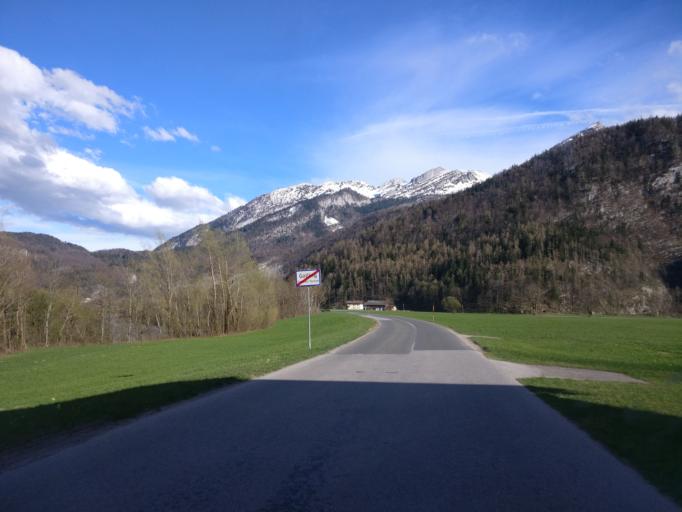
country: AT
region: Salzburg
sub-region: Politischer Bezirk Hallein
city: Golling an der Salzach
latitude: 47.5836
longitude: 13.1609
